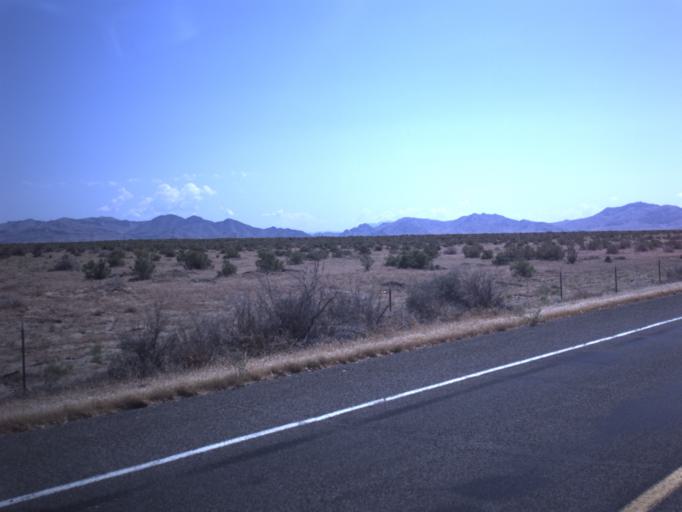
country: US
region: Utah
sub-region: Millard County
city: Delta
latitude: 39.4722
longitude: -112.4698
